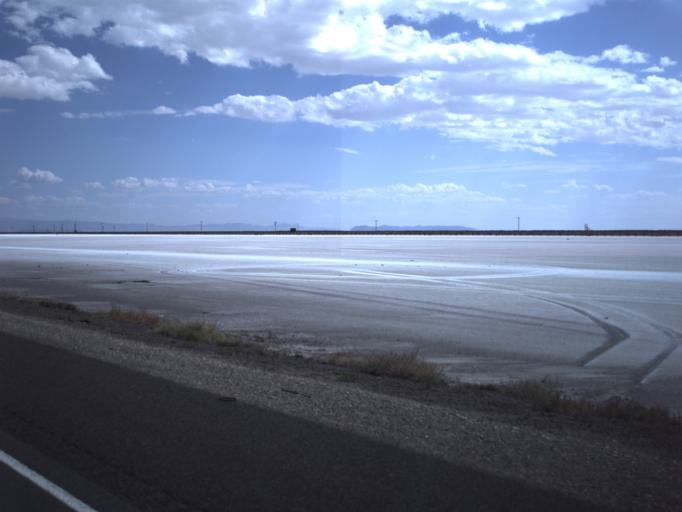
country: US
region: Utah
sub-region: Tooele County
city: Wendover
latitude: 40.7348
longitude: -113.6727
